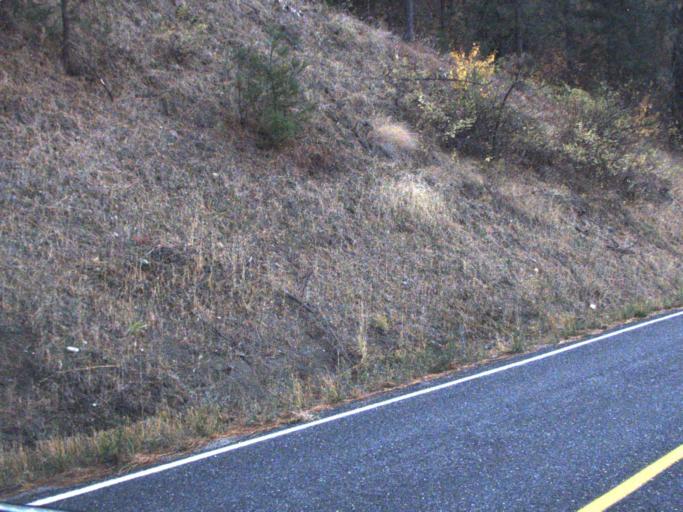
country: US
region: Washington
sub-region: Stevens County
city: Kettle Falls
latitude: 48.2339
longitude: -118.1525
